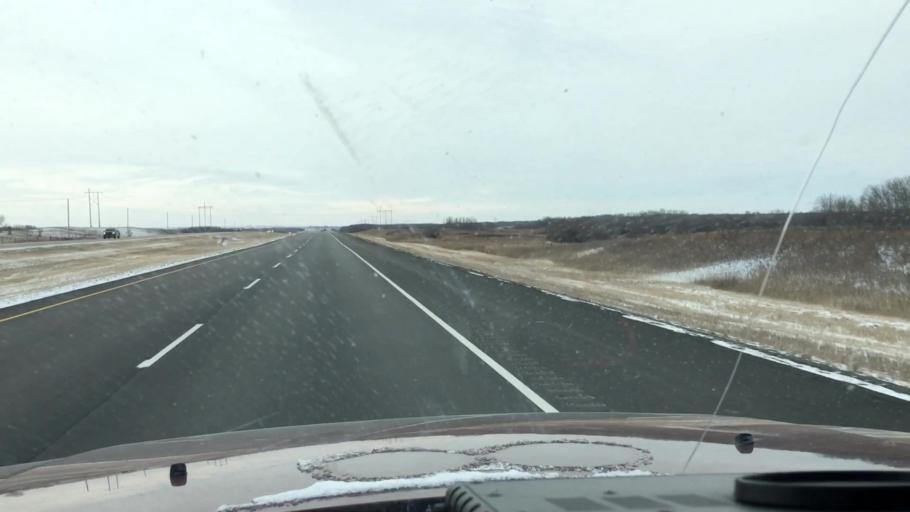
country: CA
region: Saskatchewan
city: Saskatoon
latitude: 51.8964
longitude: -106.5197
